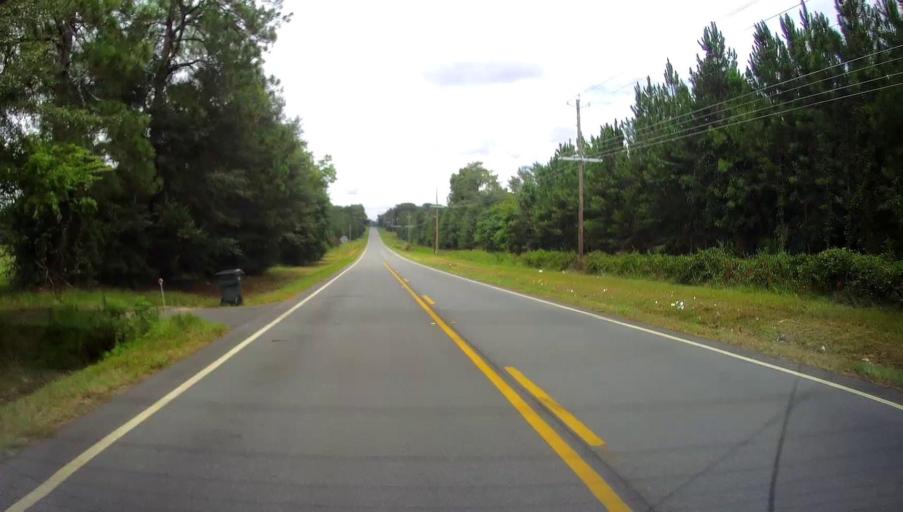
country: US
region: Georgia
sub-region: Schley County
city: Ellaville
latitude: 32.2441
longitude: -84.2871
